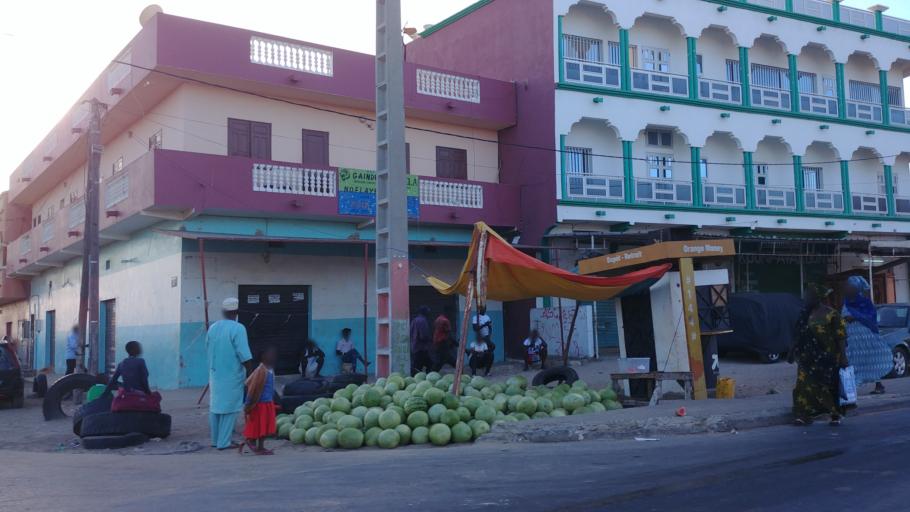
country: SN
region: Saint-Louis
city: Saint-Louis
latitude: 16.0116
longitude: -16.4960
